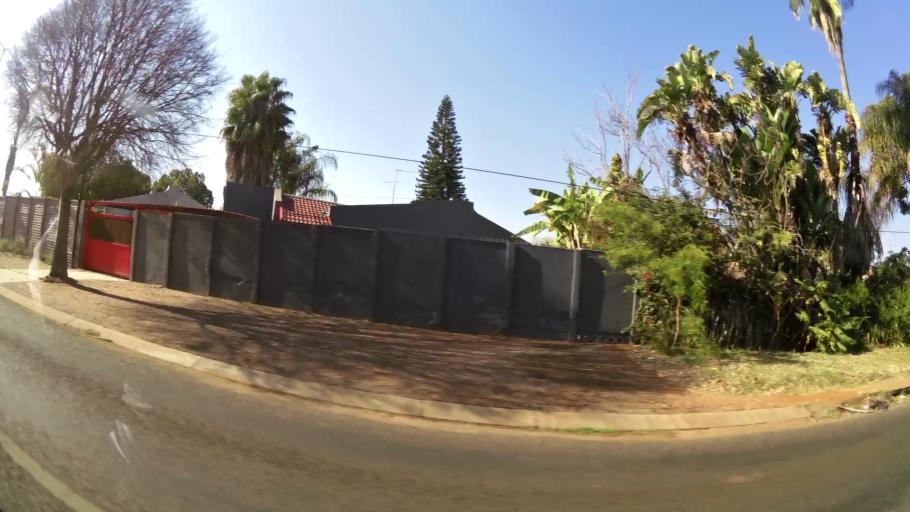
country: ZA
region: Gauteng
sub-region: City of Tshwane Metropolitan Municipality
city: Pretoria
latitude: -25.6490
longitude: 28.2317
